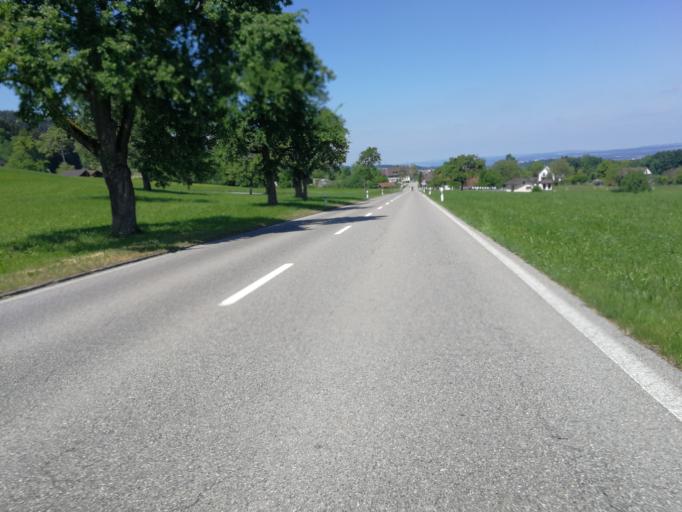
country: CH
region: Zurich
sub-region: Bezirk Uster
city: Esslingen
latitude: 47.2805
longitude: 8.6983
